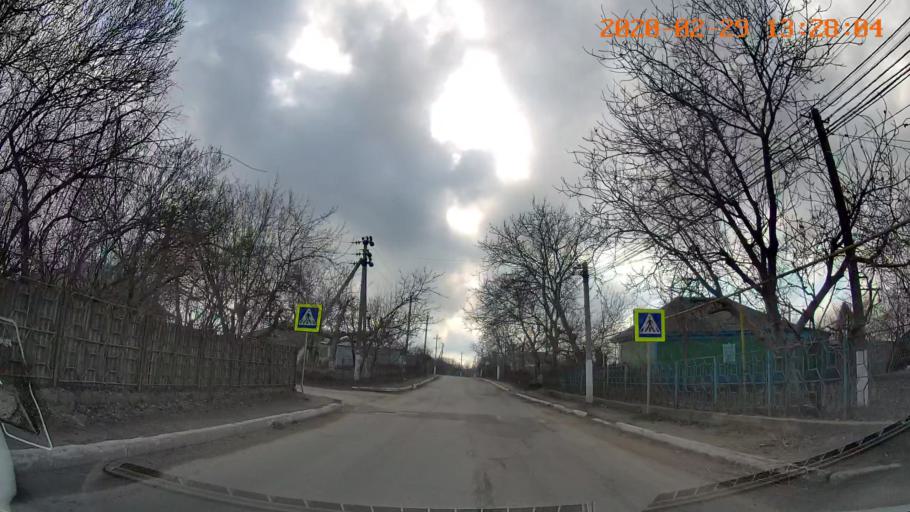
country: MD
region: Telenesti
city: Camenca
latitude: 47.9082
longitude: 28.6440
